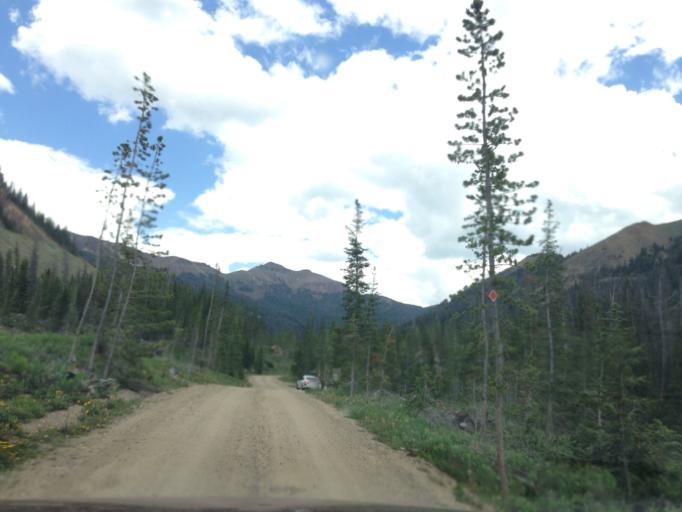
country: US
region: Colorado
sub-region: Larimer County
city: Estes Park
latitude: 40.5029
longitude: -105.9049
